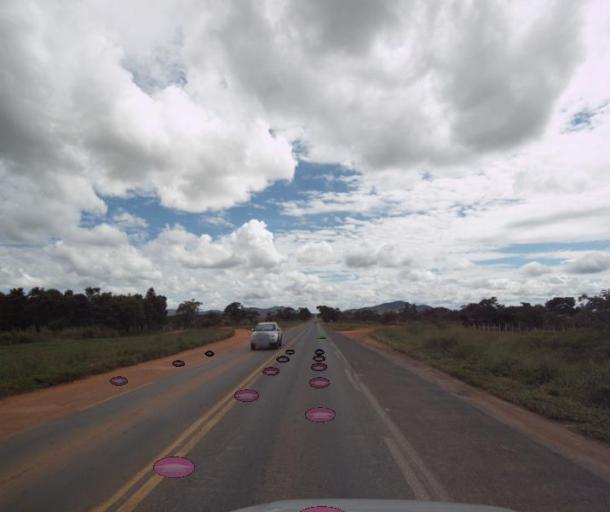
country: BR
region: Goias
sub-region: Uruacu
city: Uruacu
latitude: -14.4650
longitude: -49.1561
